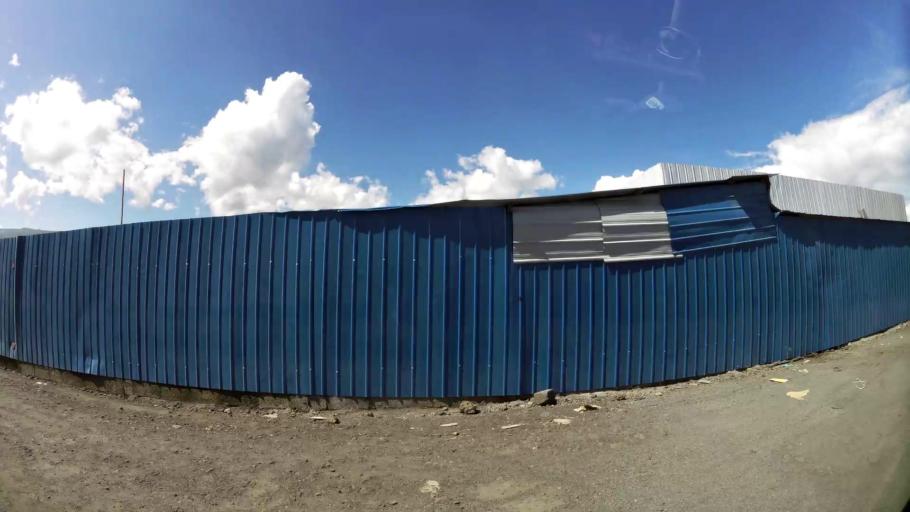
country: KM
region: Grande Comore
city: Mavingouni
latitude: -11.7233
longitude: 43.2396
